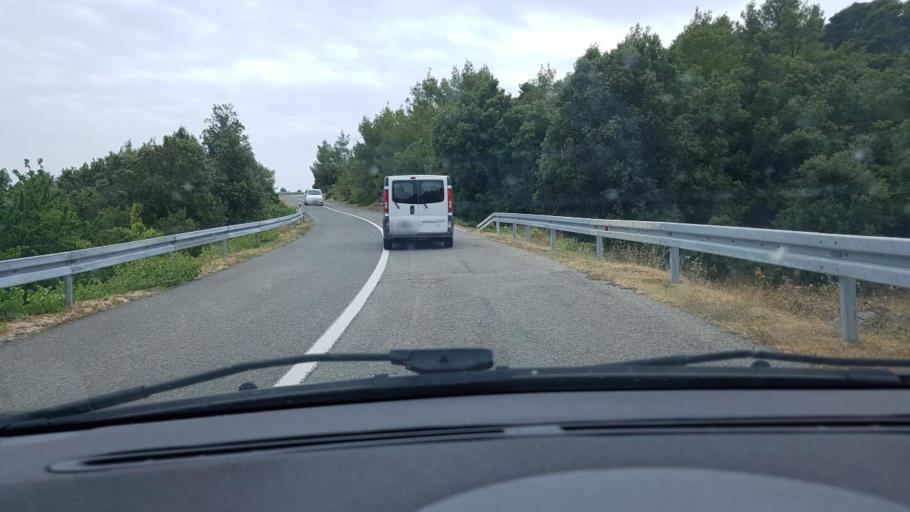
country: HR
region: Dubrovacko-Neretvanska
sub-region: Grad Korcula
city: Zrnovo
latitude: 42.9432
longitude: 17.0247
